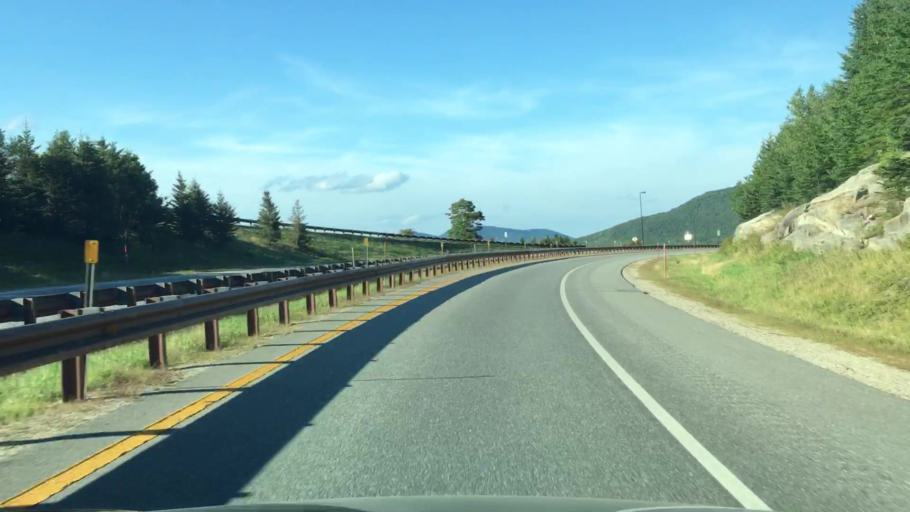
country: US
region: New Hampshire
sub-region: Grafton County
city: Deerfield
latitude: 44.1795
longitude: -71.6918
